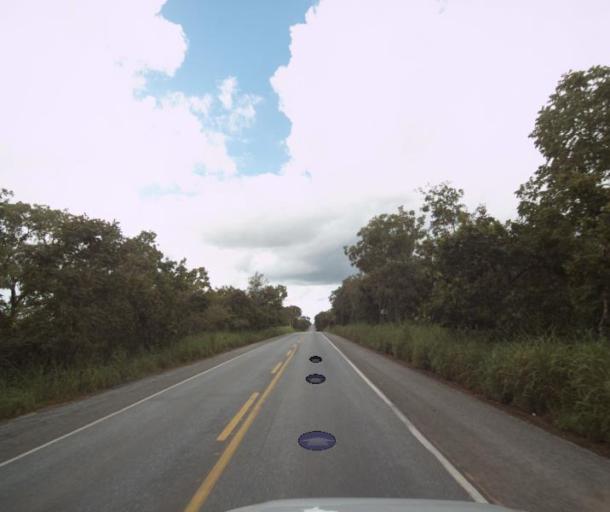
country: BR
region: Goias
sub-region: Porangatu
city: Porangatu
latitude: -13.2731
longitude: -49.1308
